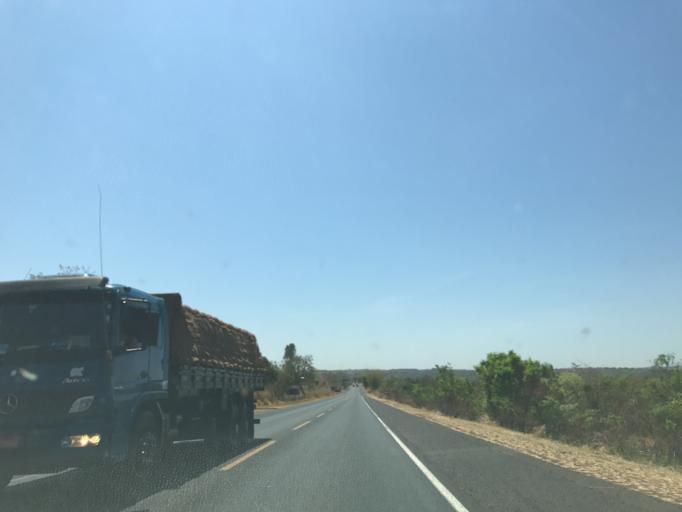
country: BR
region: Minas Gerais
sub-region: Prata
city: Prata
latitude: -19.3710
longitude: -48.8991
